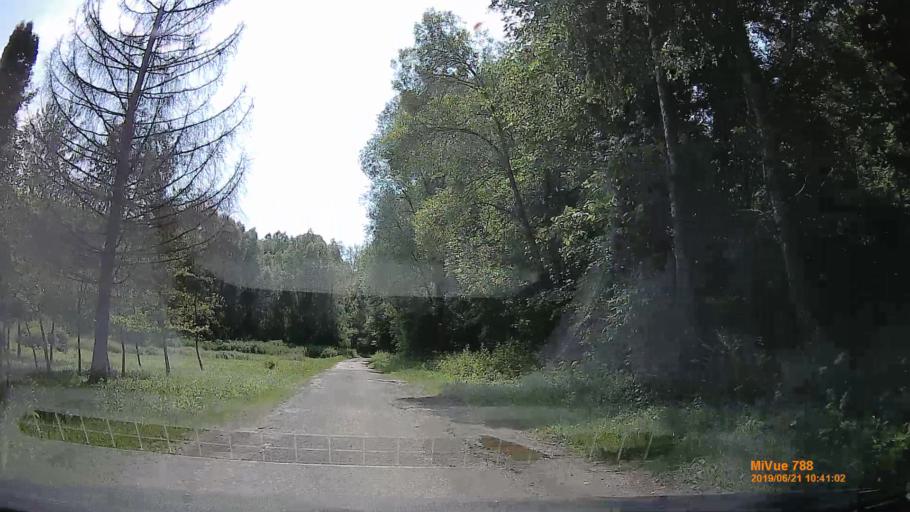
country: HU
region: Baranya
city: Buekkoesd
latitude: 46.1347
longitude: 18.0009
